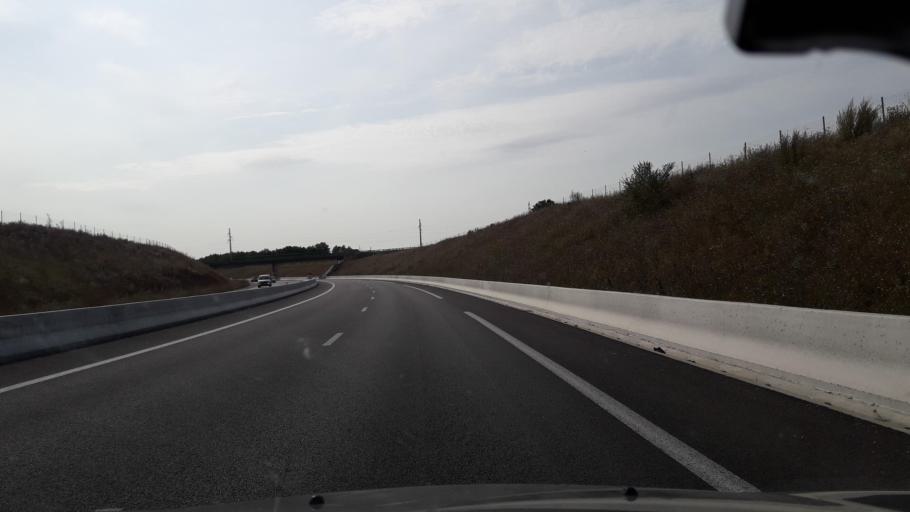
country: FR
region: Poitou-Charentes
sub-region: Departement de la Charente
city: Balzac
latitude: 45.6942
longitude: 0.0938
